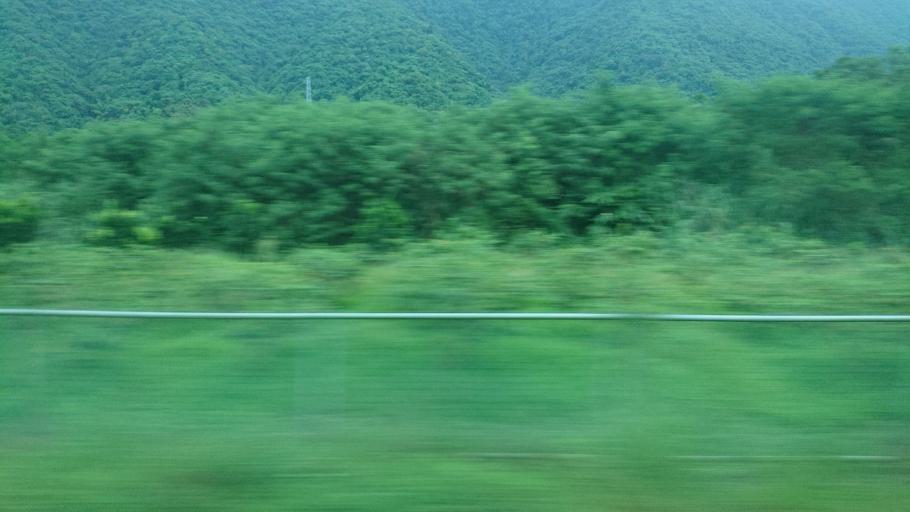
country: TW
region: Taiwan
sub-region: Hualien
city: Hualian
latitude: 24.1133
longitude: 121.6247
